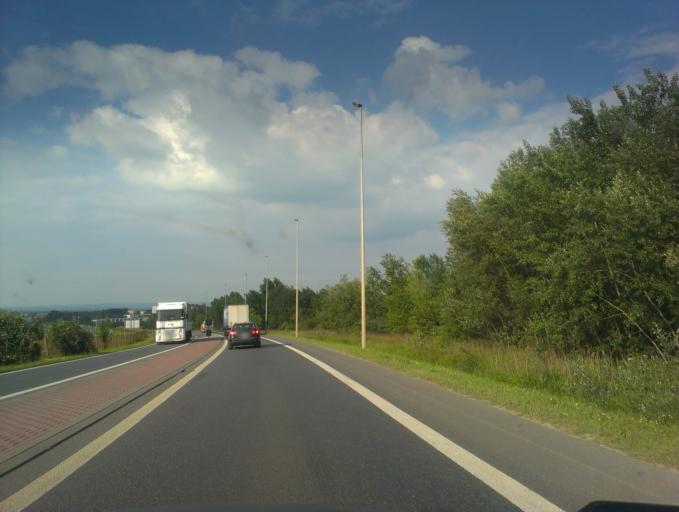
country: PL
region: Lower Silesian Voivodeship
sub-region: Powiat trzebnicki
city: Trzebnica
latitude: 51.3132
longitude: 17.0465
